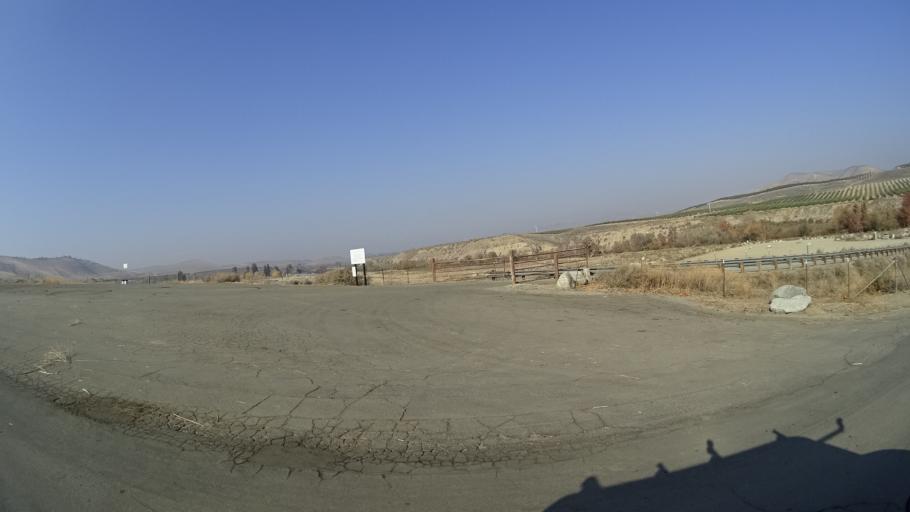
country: US
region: California
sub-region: Kern County
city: Lamont
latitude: 35.4240
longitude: -118.8304
